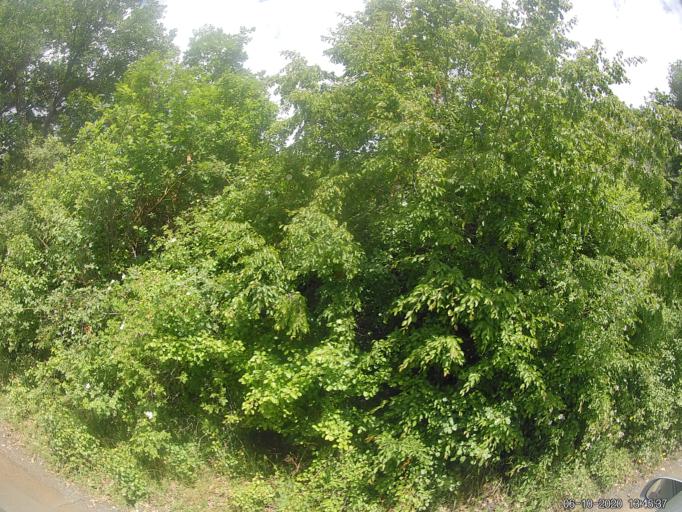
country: XK
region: Prizren
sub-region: Komuna e Therandes
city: Budakovo
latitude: 42.4106
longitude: 20.9147
